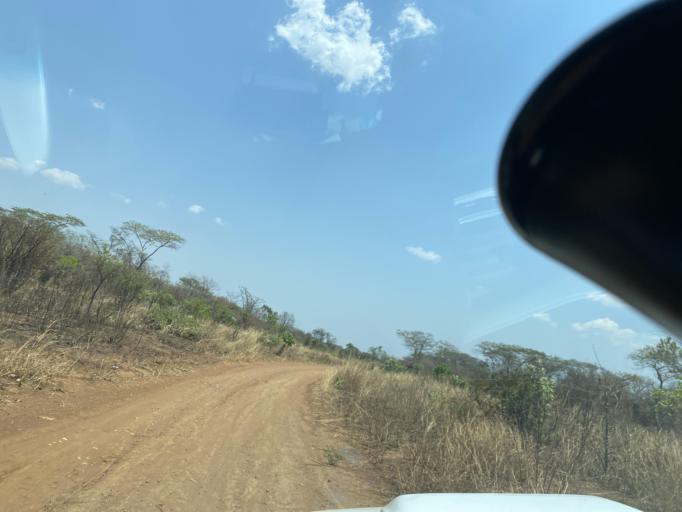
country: ZM
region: Lusaka
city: Lusaka
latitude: -15.5064
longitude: 28.0082
